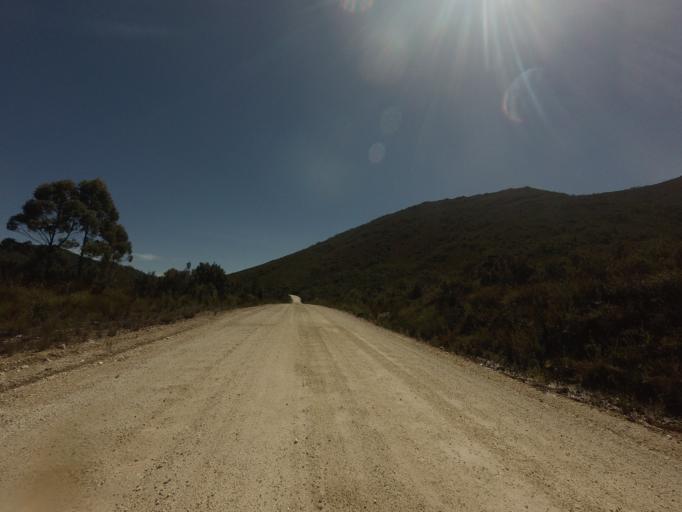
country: AU
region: Tasmania
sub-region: Huon Valley
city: Geeveston
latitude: -42.9368
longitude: 146.3475
